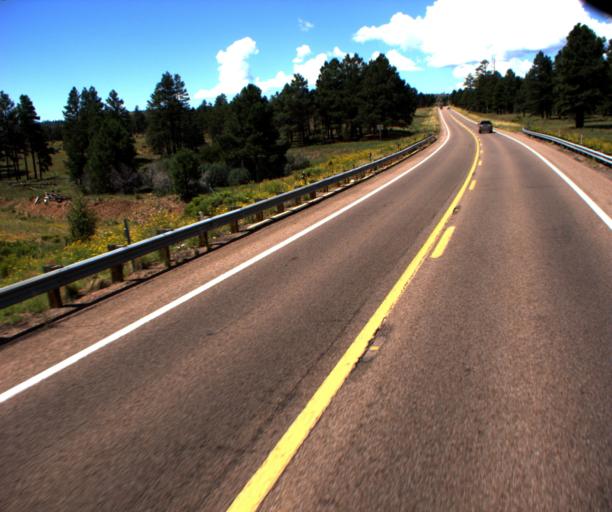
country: US
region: Arizona
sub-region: Navajo County
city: Heber-Overgaard
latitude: 34.3688
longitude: -110.4311
